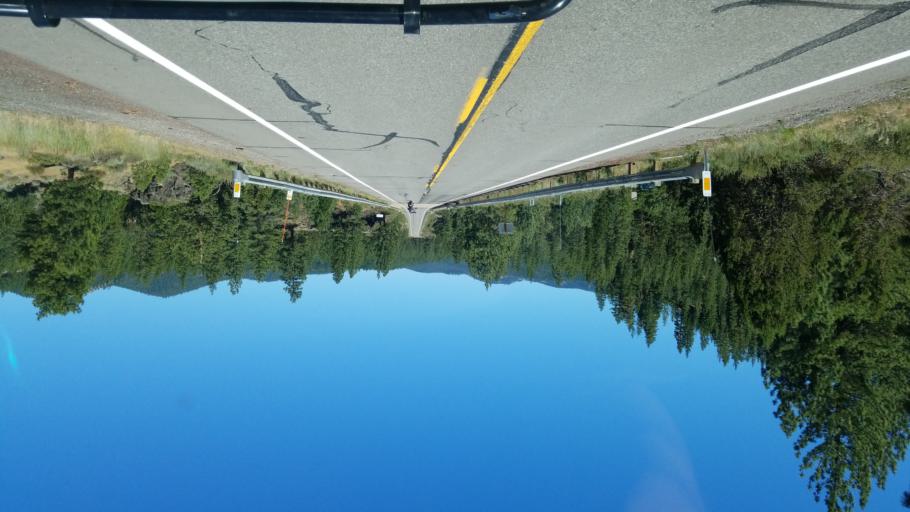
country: US
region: California
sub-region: Lassen County
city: Susanville
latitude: 40.3964
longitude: -120.7787
